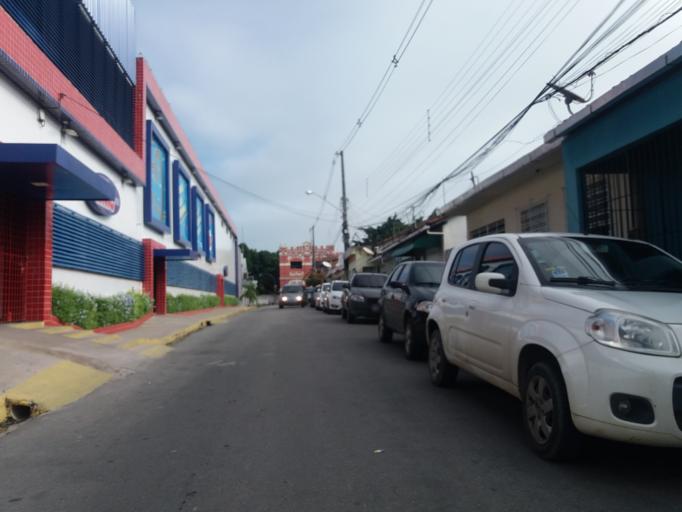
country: BR
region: Pernambuco
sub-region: Paulista
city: Paulista
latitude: -7.9388
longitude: -34.8832
